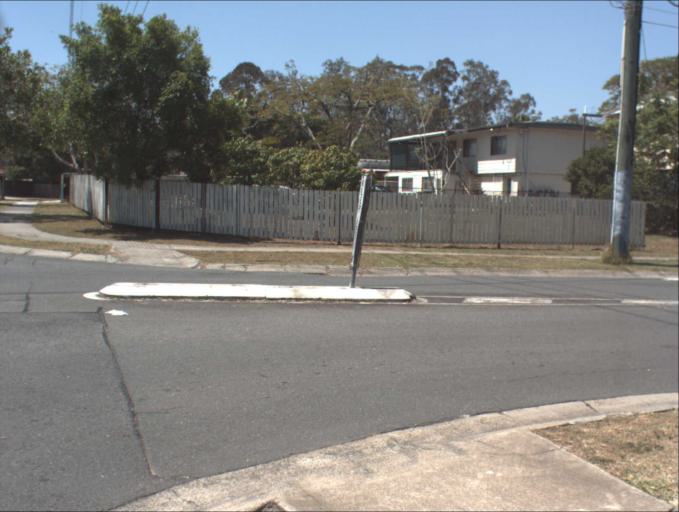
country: AU
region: Queensland
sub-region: Logan
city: Beenleigh
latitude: -27.6887
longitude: 153.1798
